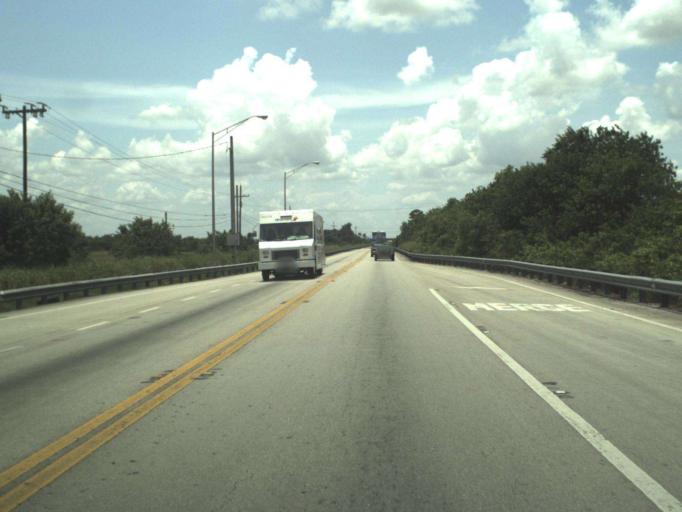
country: US
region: Florida
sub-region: Saint Lucie County
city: Lakewood Park
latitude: 27.4690
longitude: -80.3991
